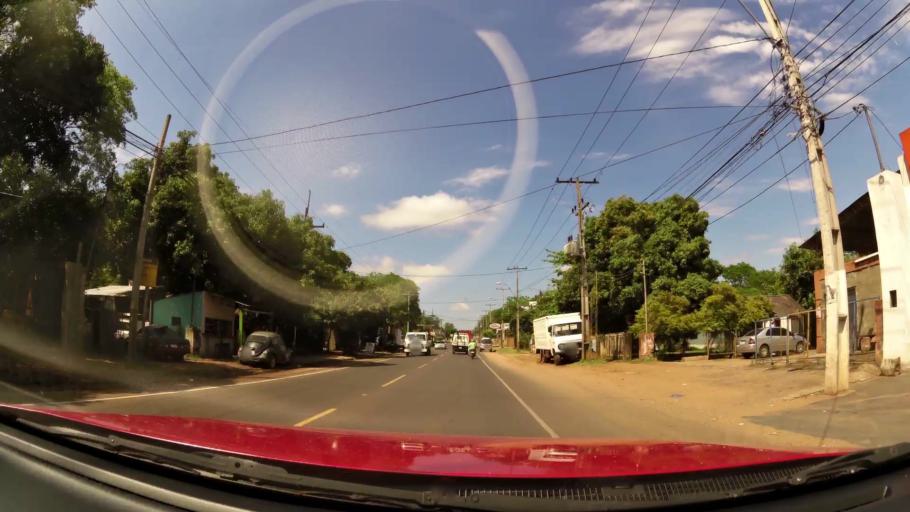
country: PY
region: Central
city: San Lorenzo
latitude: -25.2796
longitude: -57.4980
